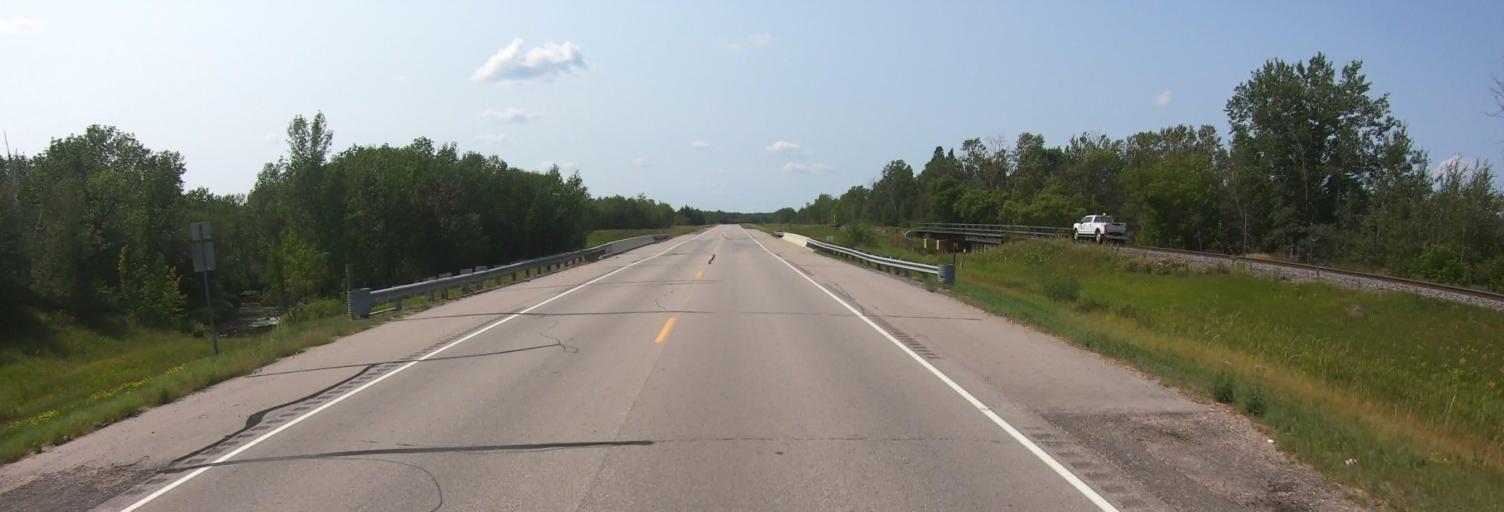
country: US
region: Minnesota
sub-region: Lake of the Woods County
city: Baudette
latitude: 48.7109
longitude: -94.6971
